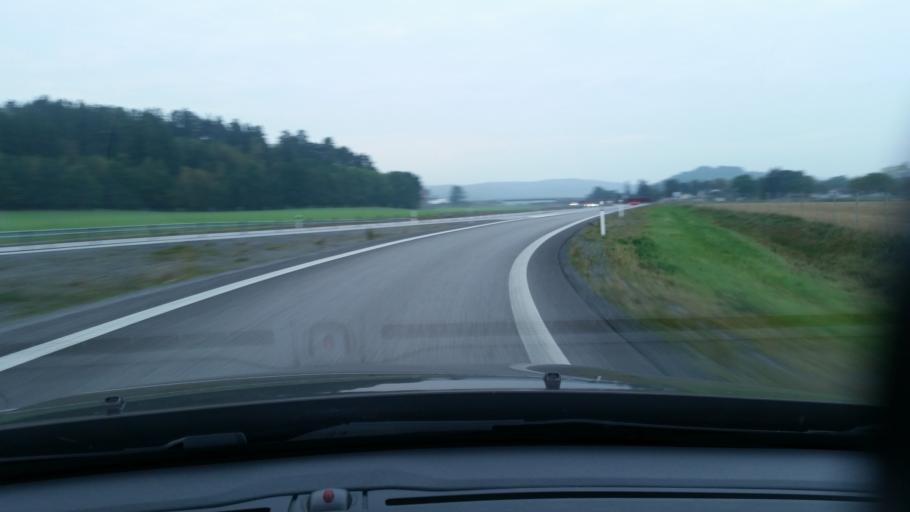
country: SE
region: Vaestra Goetaland
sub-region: Lilla Edets Kommun
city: Lodose
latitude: 58.0102
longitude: 12.1648
